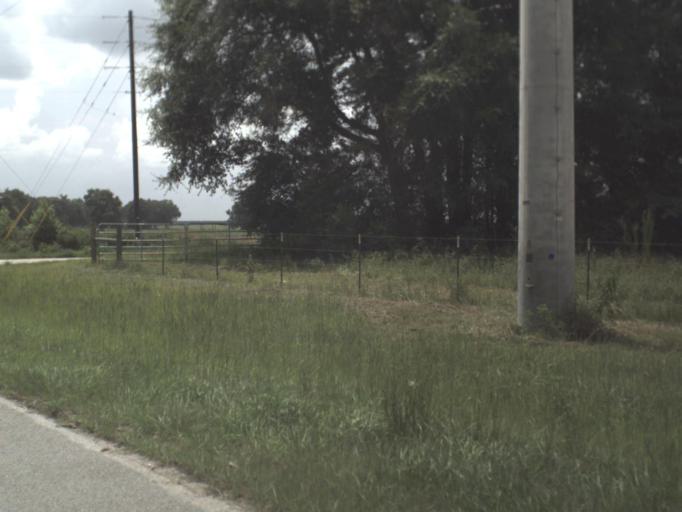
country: US
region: Florida
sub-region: Madison County
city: Madison
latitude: 30.4731
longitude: -83.2659
